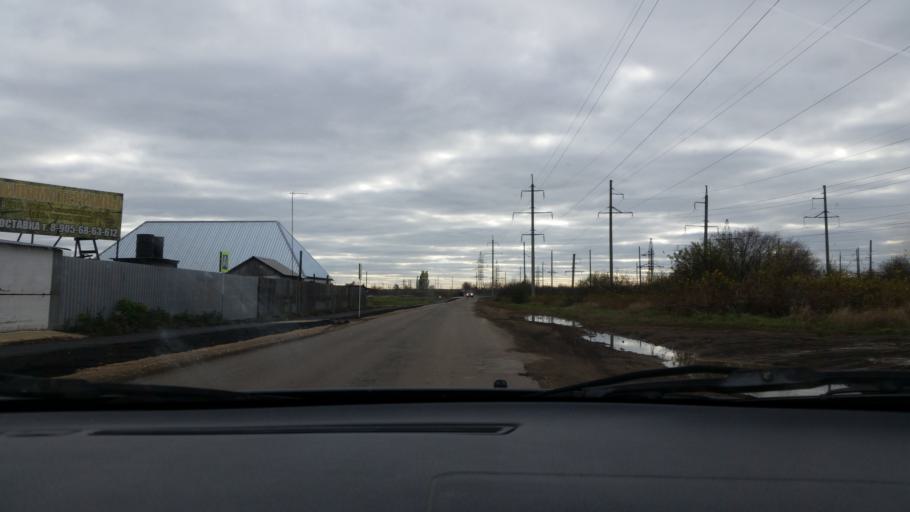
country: RU
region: Lipetsk
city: Gryazi
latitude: 52.4695
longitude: 39.9434
